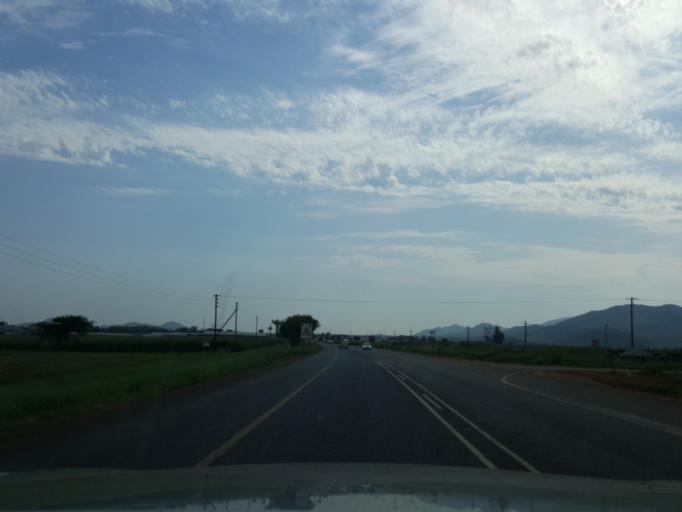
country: SZ
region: Hhohho
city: Ntfonjeni
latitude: -25.5043
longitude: 31.4984
